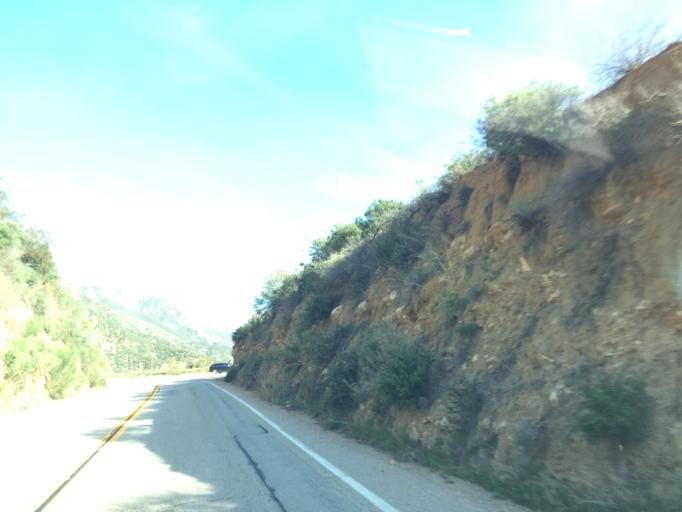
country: US
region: California
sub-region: San Bernardino County
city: San Antonio Heights
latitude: 34.1775
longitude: -117.6766
